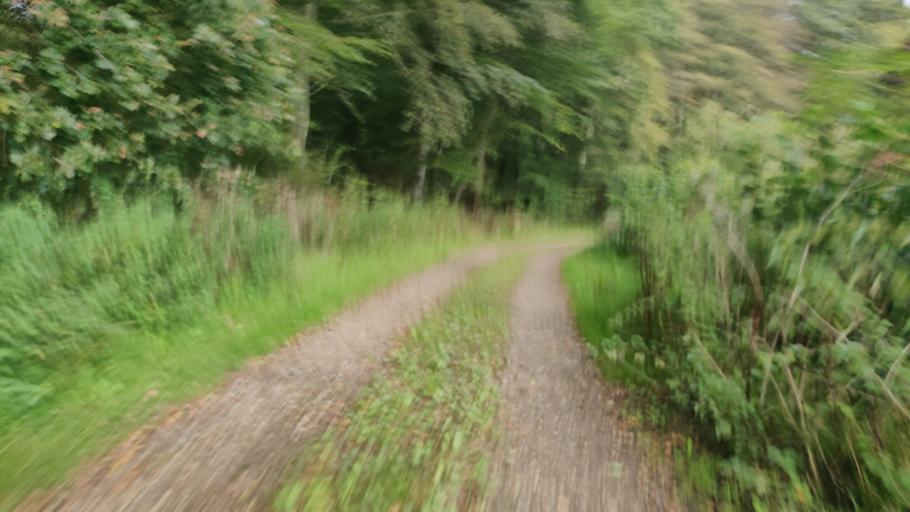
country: DK
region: South Denmark
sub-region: Kolding Kommune
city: Lunderskov
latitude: 55.5419
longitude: 9.3665
